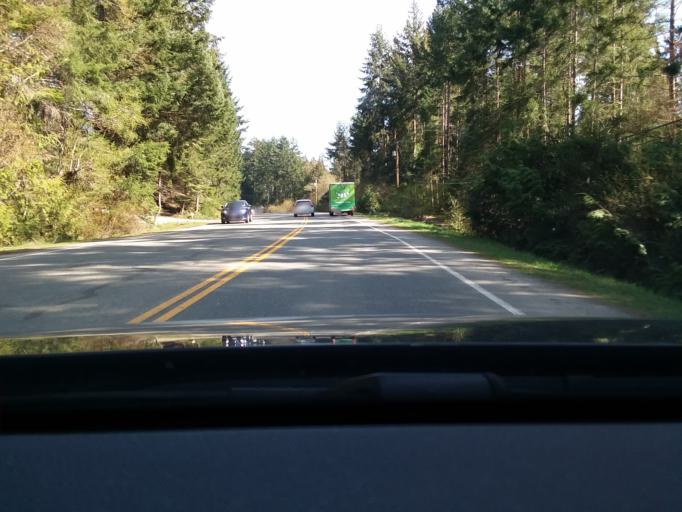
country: CA
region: British Columbia
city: North Saanich
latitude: 48.8522
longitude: -123.4607
